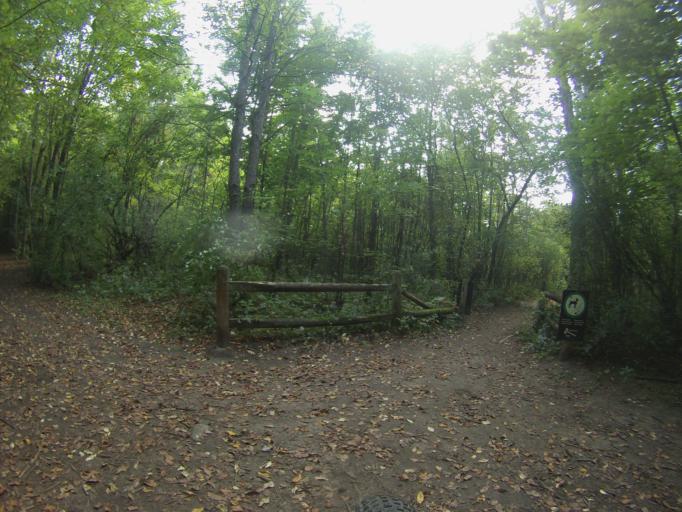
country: CA
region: Ontario
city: Ottawa
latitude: 45.3557
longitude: -75.6220
